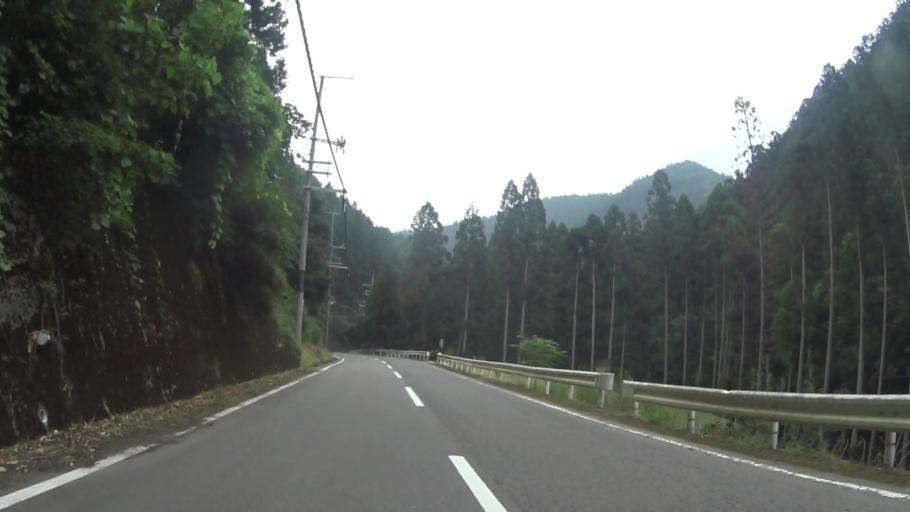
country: JP
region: Kyoto
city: Kameoka
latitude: 35.1482
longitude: 135.5923
